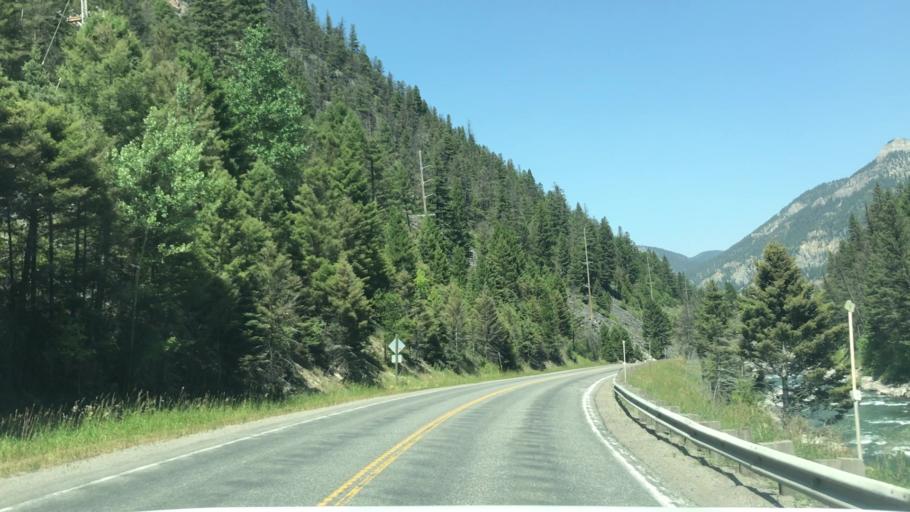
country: US
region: Montana
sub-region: Gallatin County
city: Big Sky
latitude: 45.4221
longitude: -111.2341
